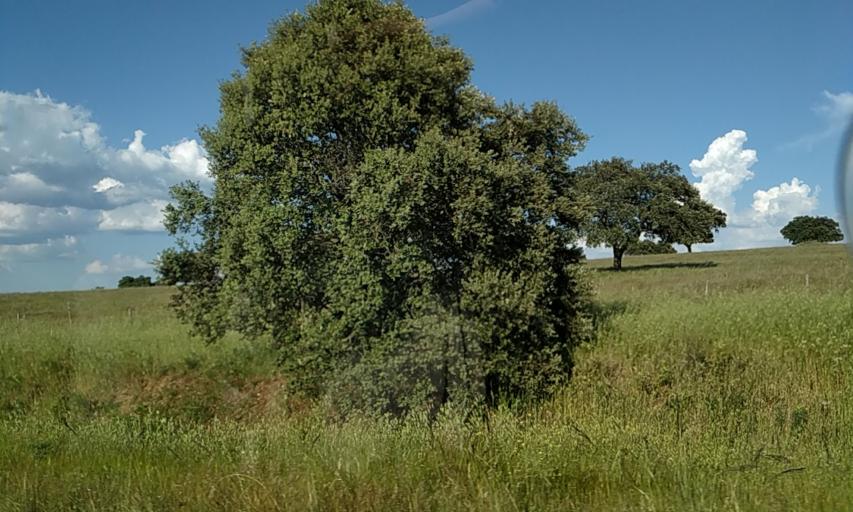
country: PT
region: Portalegre
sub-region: Portalegre
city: Urra
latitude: 39.1115
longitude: -7.4400
